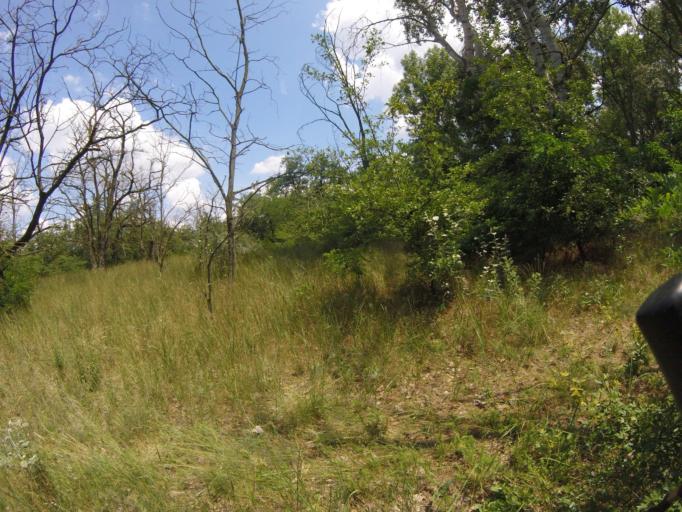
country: HU
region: Pest
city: Csemo
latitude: 47.0737
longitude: 19.7267
